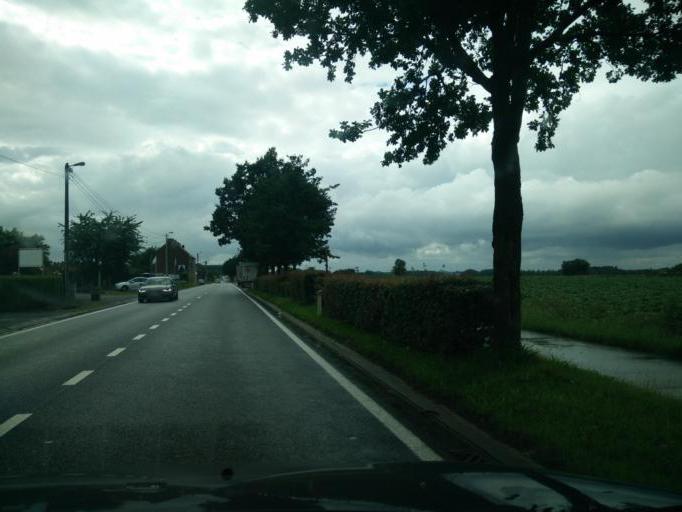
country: BE
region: Flanders
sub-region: Provincie Vlaams-Brabant
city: Halle
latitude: 50.7443
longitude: 4.2008
